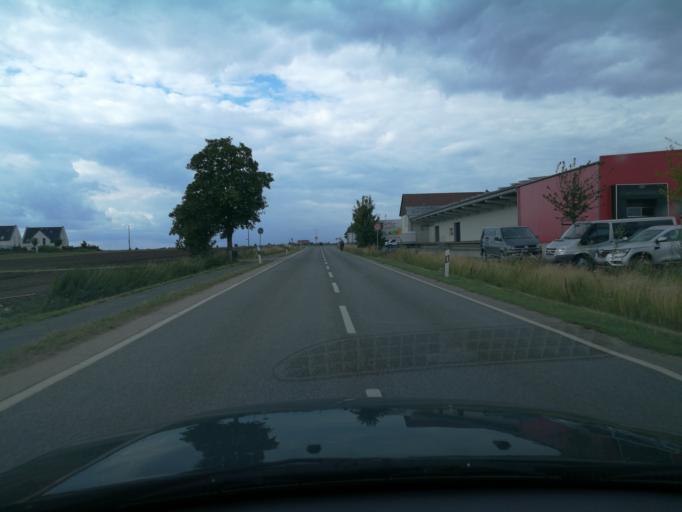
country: DE
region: Bavaria
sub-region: Regierungsbezirk Mittelfranken
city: Wetzendorf
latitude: 49.4891
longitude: 11.0367
